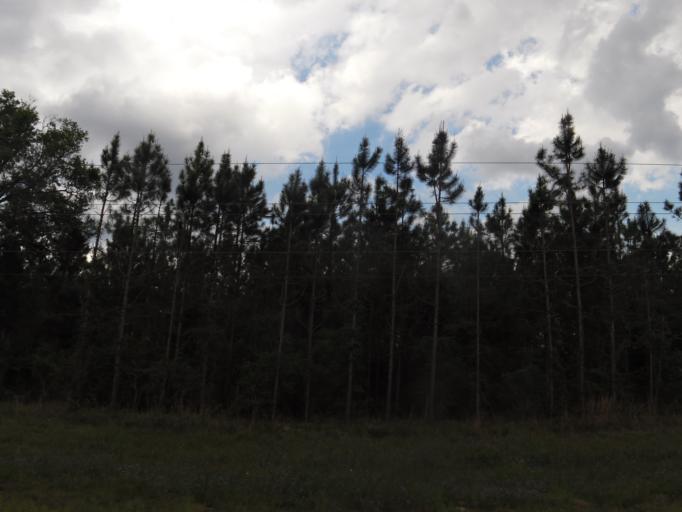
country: US
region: Georgia
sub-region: Charlton County
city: Folkston
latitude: 30.8379
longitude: -81.8953
